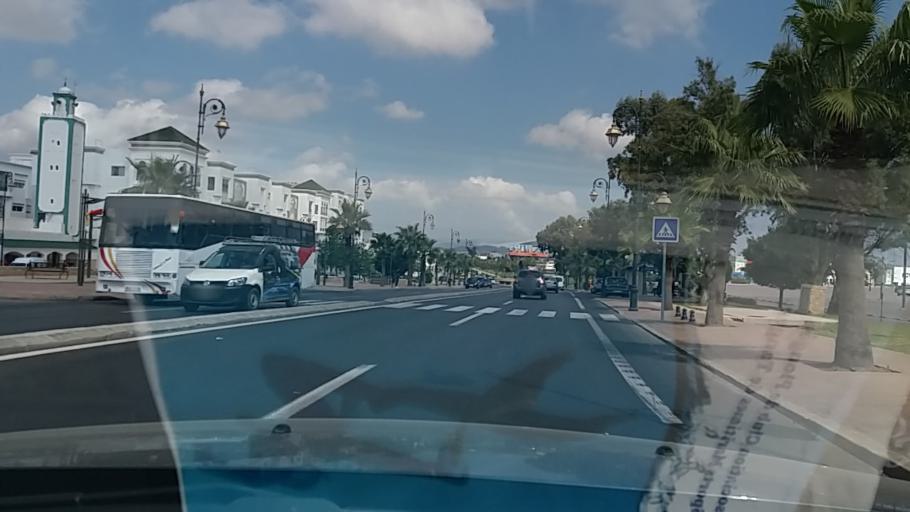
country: MA
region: Tanger-Tetouan
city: Tetouan
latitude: 35.6022
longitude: -5.3365
